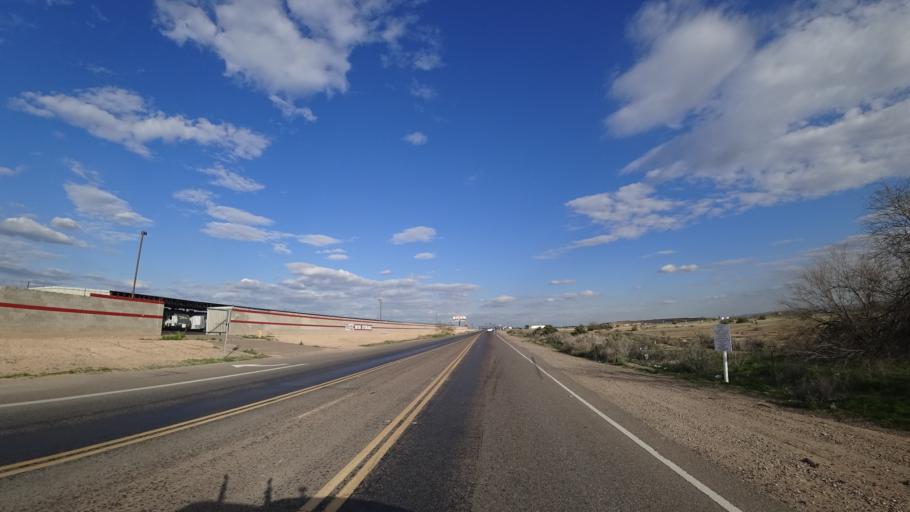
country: US
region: Arizona
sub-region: Maricopa County
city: Youngtown
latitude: 33.5510
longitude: -112.3288
